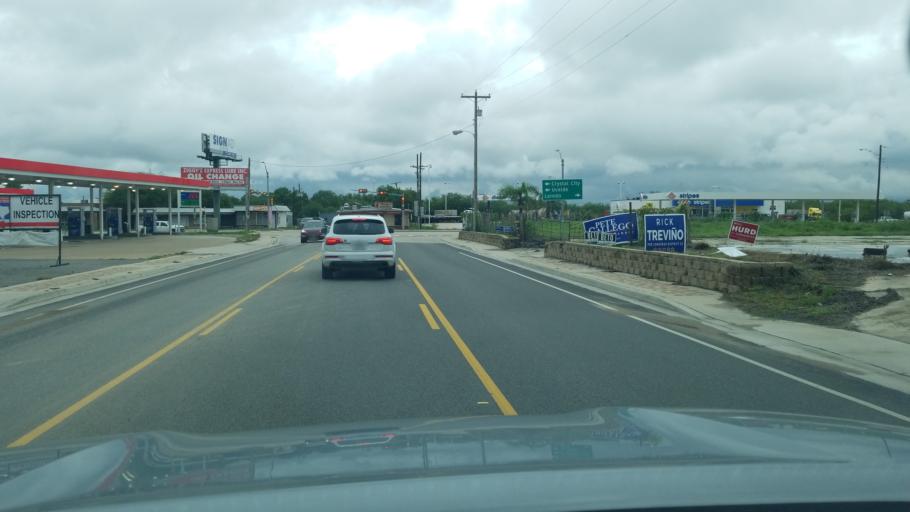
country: US
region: Texas
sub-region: Dimmit County
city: Carrizo Springs
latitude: 28.5213
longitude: -99.8583
